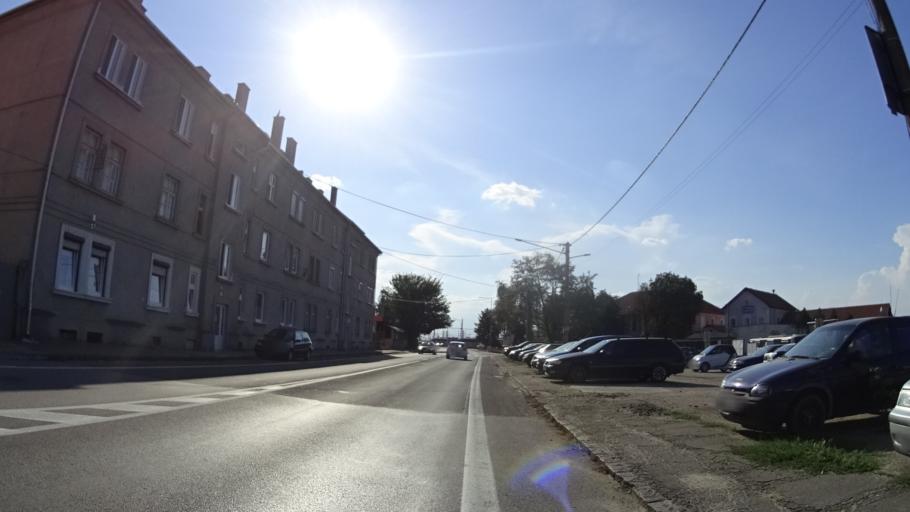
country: SK
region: Nitriansky
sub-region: Okres Nove Zamky
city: Sturovo
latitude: 47.7990
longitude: 18.6805
